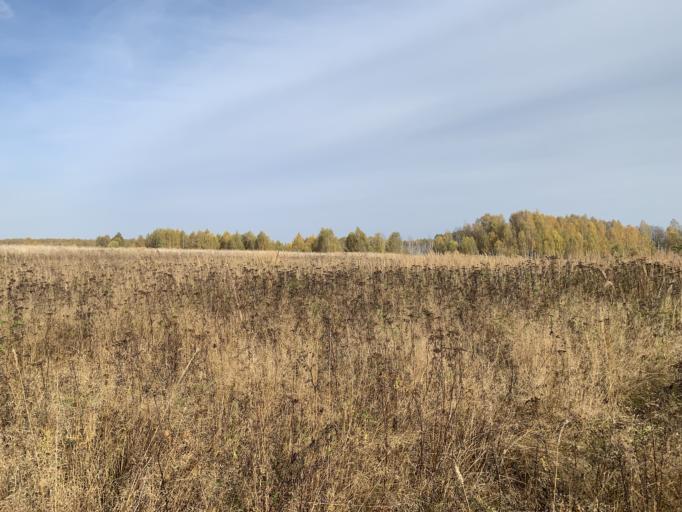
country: RU
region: Jaroslavl
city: Porech'ye-Rybnoye
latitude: 57.0034
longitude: 39.4030
